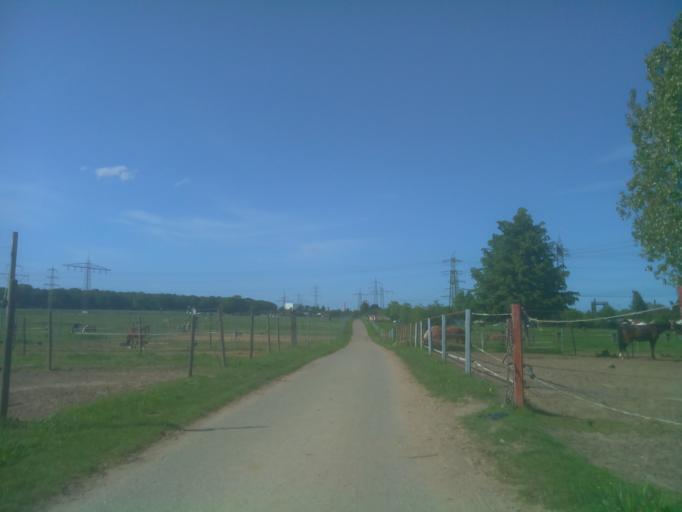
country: DE
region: Baden-Wuerttemberg
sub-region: Karlsruhe Region
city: Plankstadt
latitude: 49.4282
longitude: 8.5680
